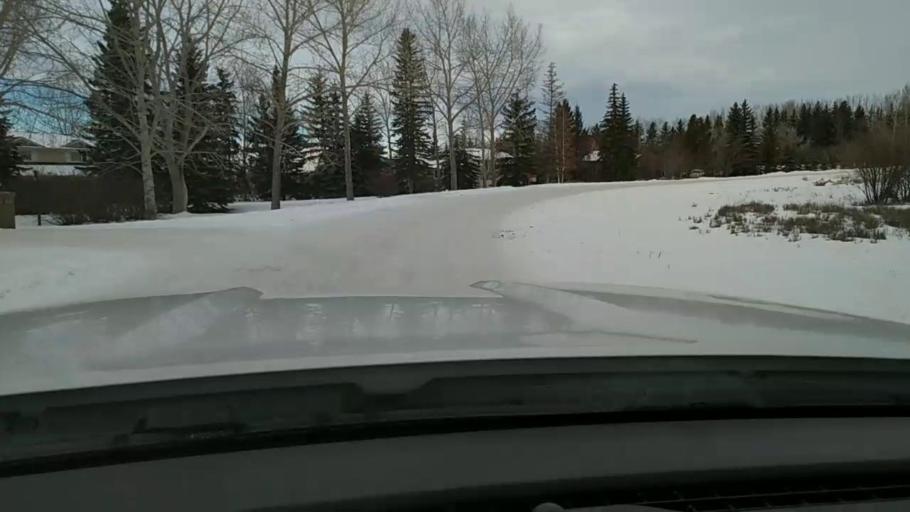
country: CA
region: Alberta
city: Calgary
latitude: 51.1163
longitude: -114.2662
